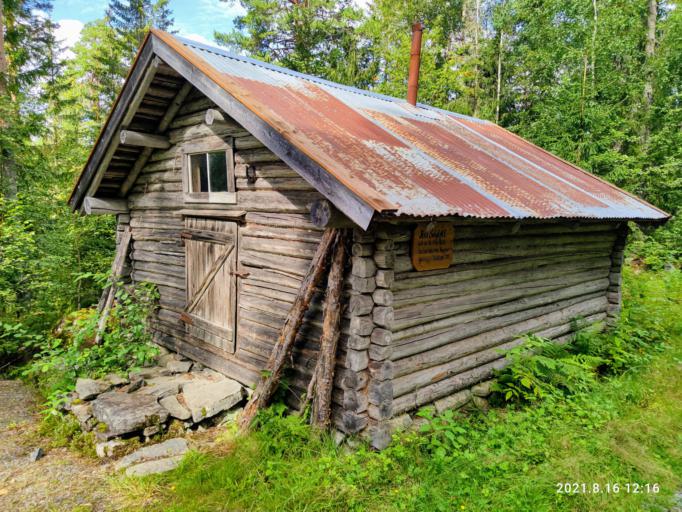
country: NO
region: Hedmark
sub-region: Sor-Odal
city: Skarnes
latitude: 60.2660
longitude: 11.6783
